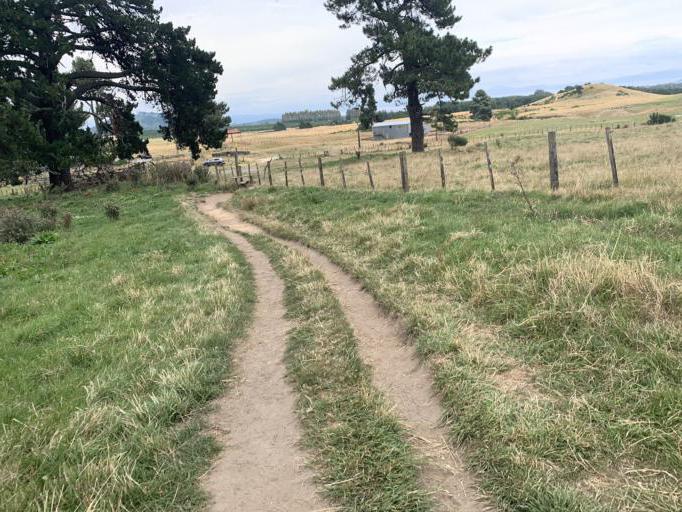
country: NZ
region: Waikato
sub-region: Taupo District
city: Taupo
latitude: -38.7034
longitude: 176.1408
